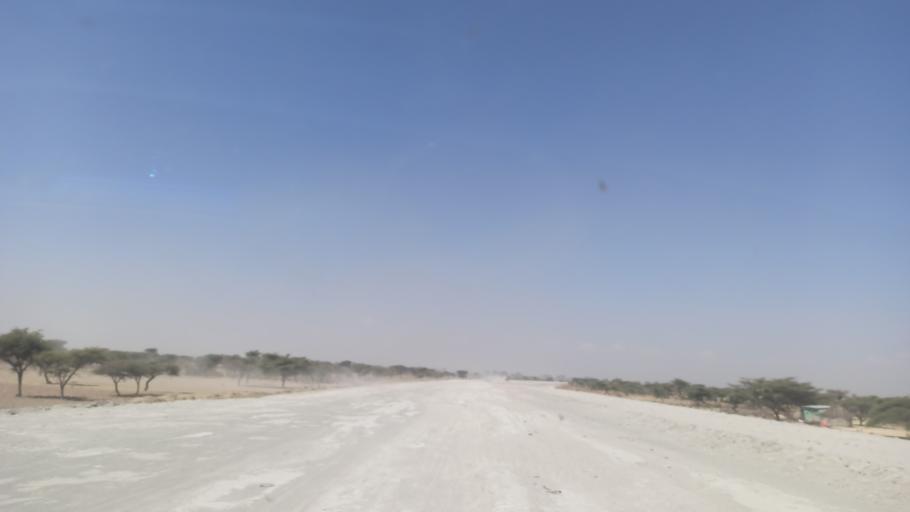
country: ET
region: Oromiya
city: Ziway
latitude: 7.6923
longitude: 38.6547
